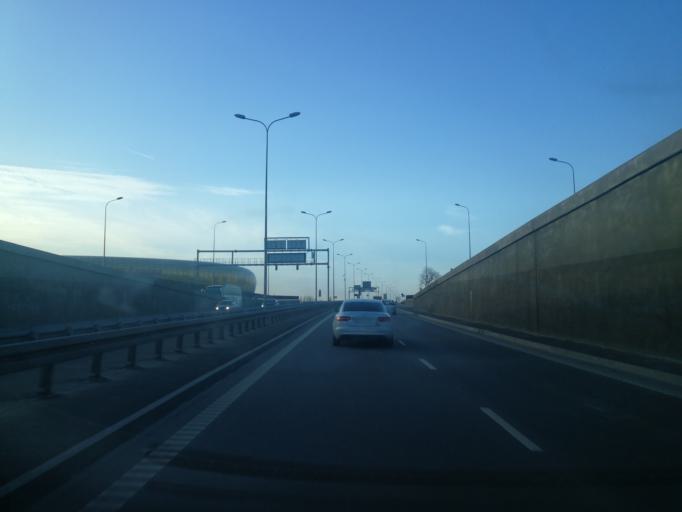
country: PL
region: Pomeranian Voivodeship
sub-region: Gdansk
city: Gdansk
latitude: 54.3891
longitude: 18.6485
